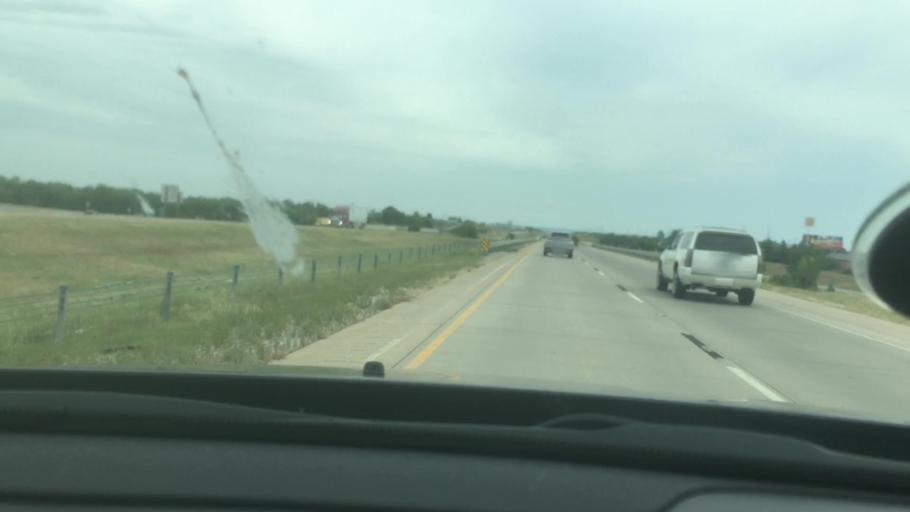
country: US
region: Oklahoma
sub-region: Carter County
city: Ardmore
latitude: 34.1999
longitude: -97.1638
